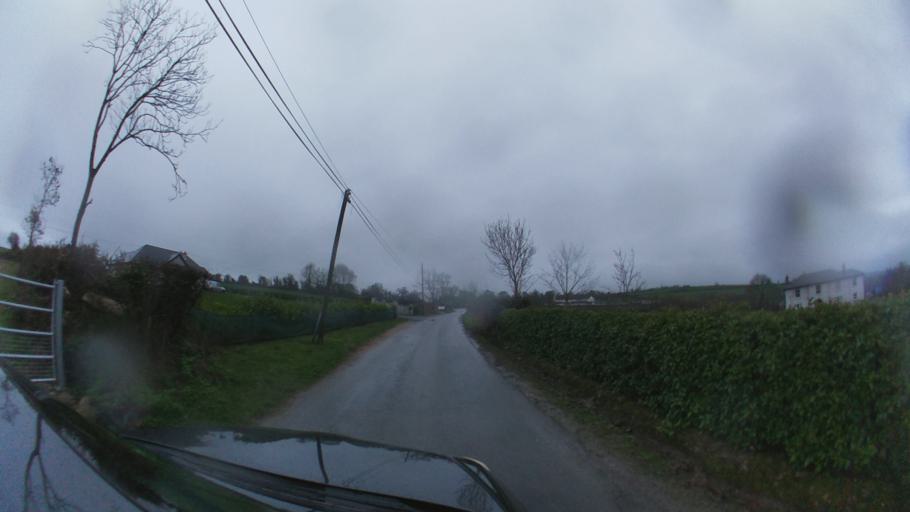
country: IE
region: Leinster
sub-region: Kilkenny
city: Graiguenamanagh
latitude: 52.5951
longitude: -6.9930
